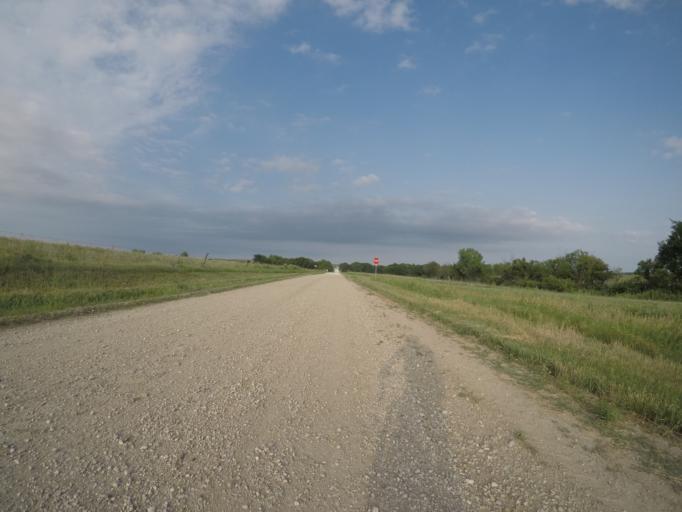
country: US
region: Kansas
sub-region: Wabaunsee County
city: Alma
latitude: 39.1015
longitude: -96.3537
